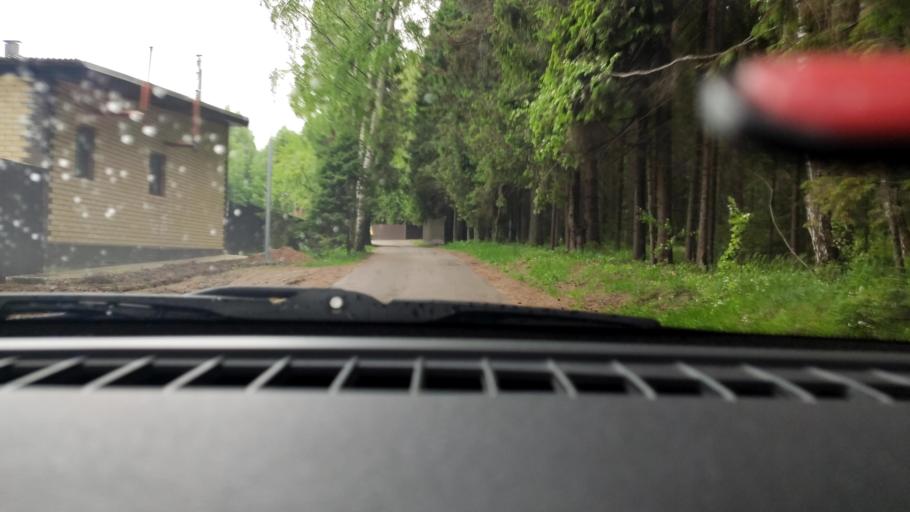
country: RU
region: Perm
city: Karagay
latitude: 58.2375
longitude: 54.8728
